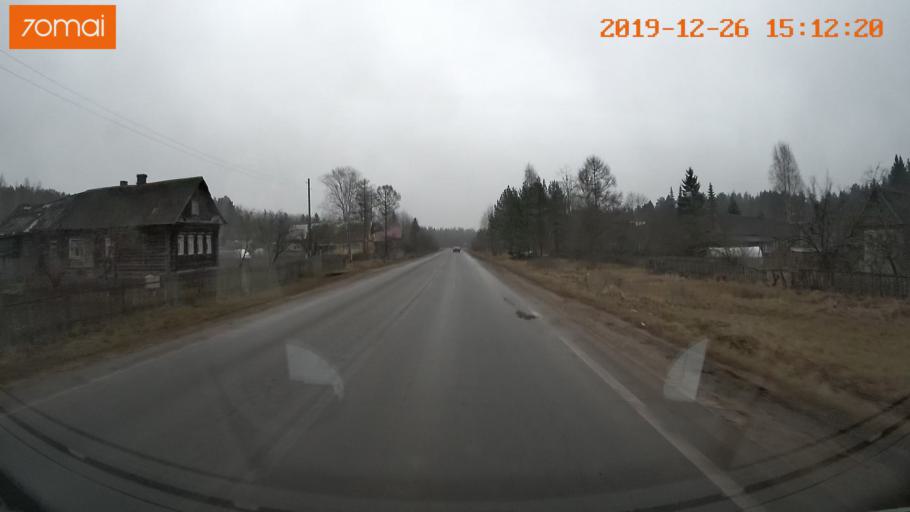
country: RU
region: Jaroslavl
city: Rybinsk
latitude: 58.1283
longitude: 38.8736
